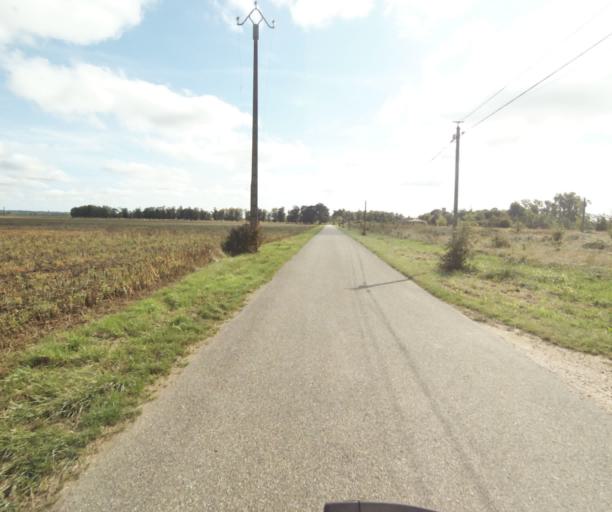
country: FR
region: Midi-Pyrenees
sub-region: Departement du Tarn-et-Garonne
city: Finhan
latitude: 43.9315
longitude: 1.2159
